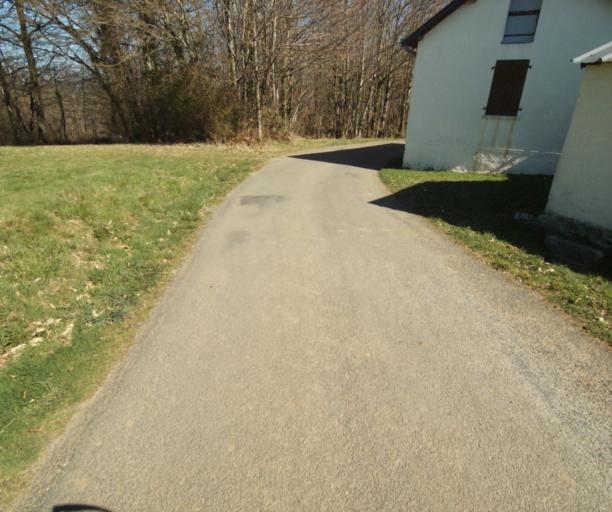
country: FR
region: Limousin
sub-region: Departement de la Correze
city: Chamboulive
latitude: 45.4104
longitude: 1.6479
